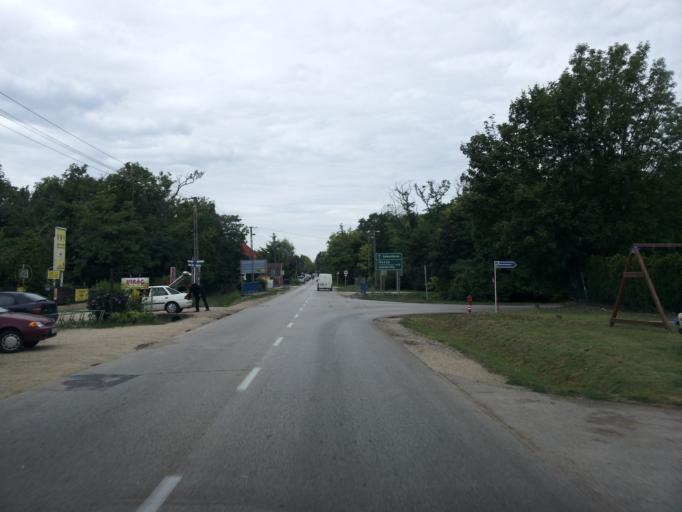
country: HU
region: Fejer
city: Velence
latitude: 47.2417
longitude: 18.6409
